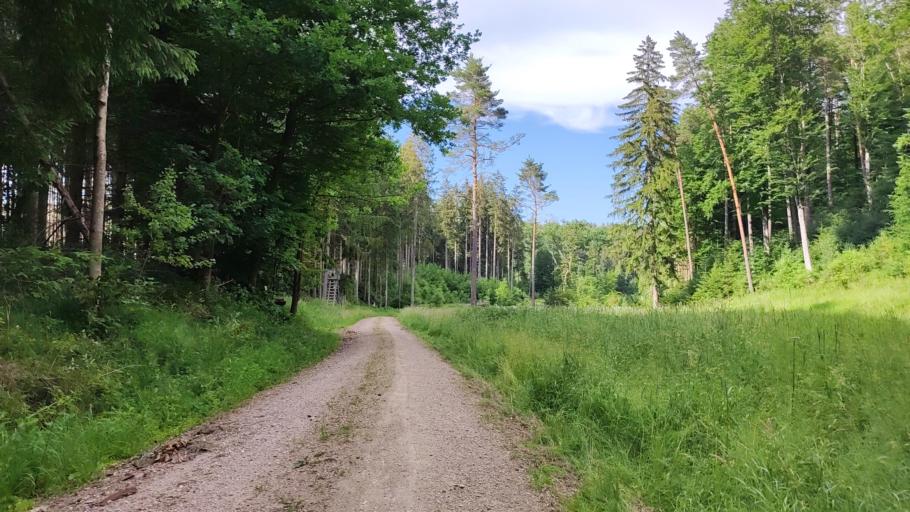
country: DE
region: Bavaria
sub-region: Swabia
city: Zusmarshausen
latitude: 48.4237
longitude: 10.5654
